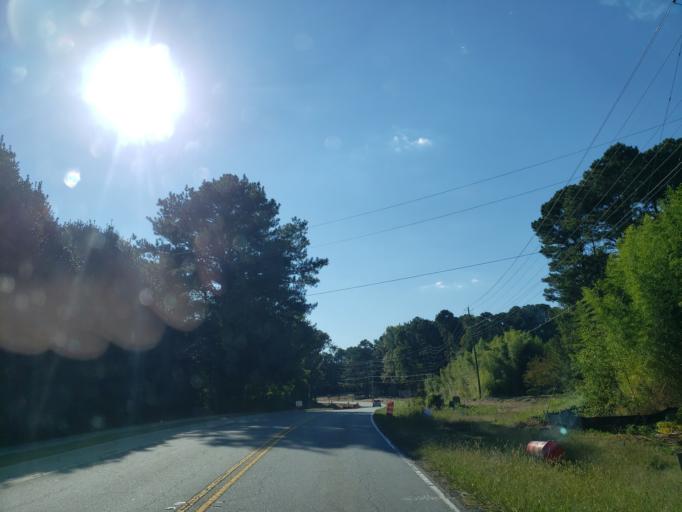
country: US
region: Georgia
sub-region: Cobb County
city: Kennesaw
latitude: 34.0298
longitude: -84.5871
